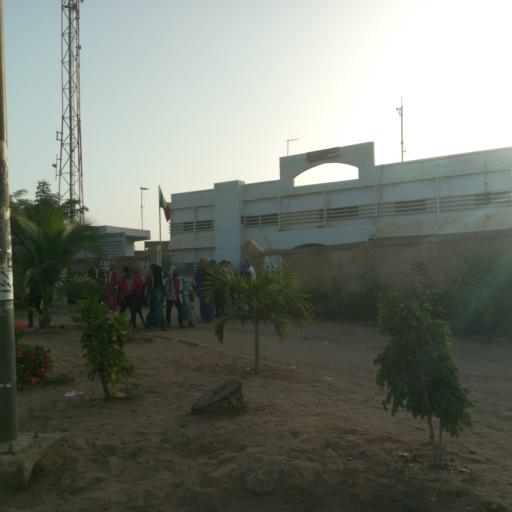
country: SN
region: Dakar
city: Dakar
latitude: 14.6968
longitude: -17.4513
